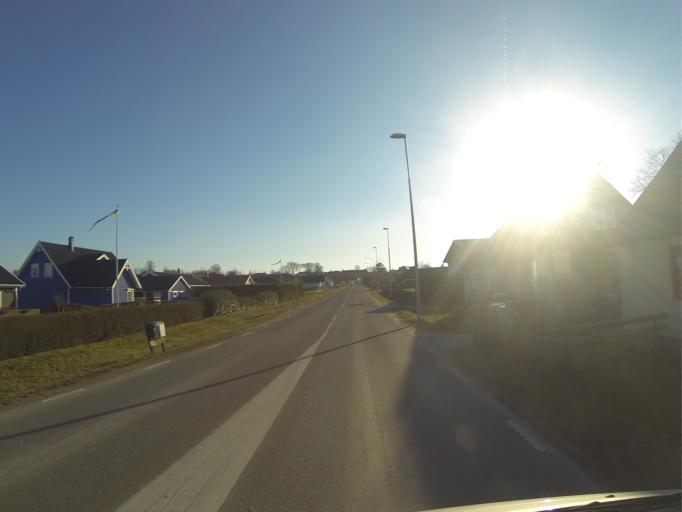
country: SE
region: Skane
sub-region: Hoors Kommun
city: Loberod
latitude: 55.7794
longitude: 13.5202
